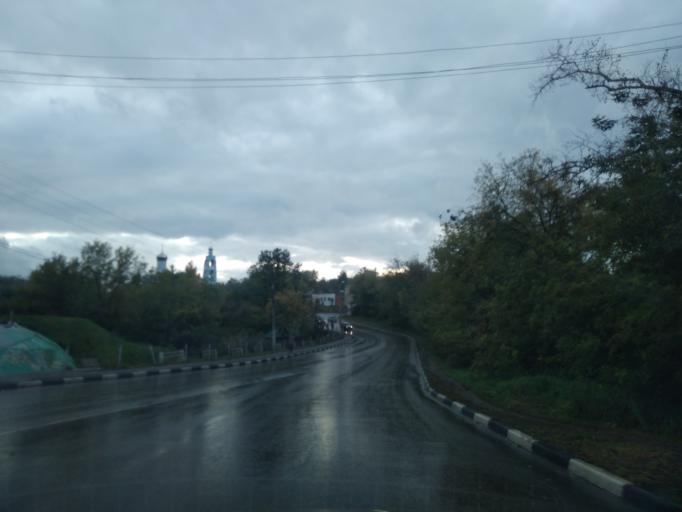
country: RU
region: Tula
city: Yefremov
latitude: 53.1373
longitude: 38.1171
